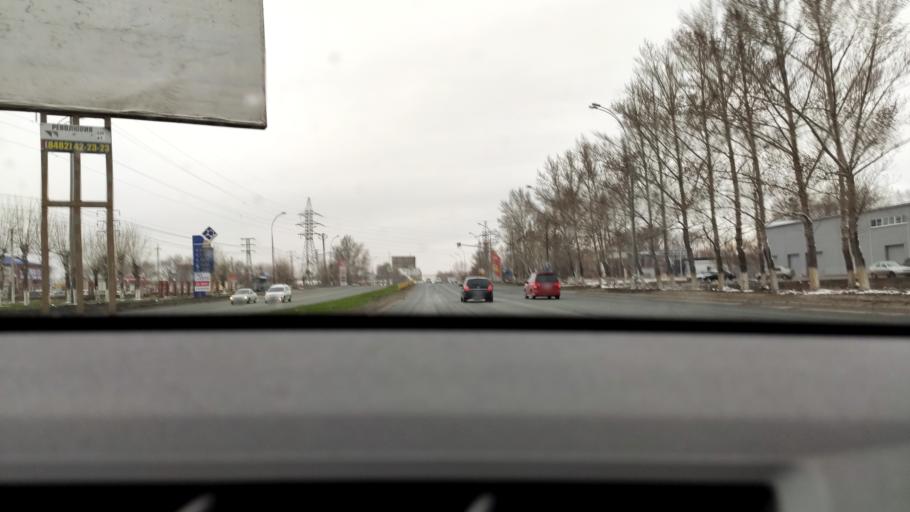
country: RU
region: Samara
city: Tol'yatti
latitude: 53.5491
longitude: 49.2879
